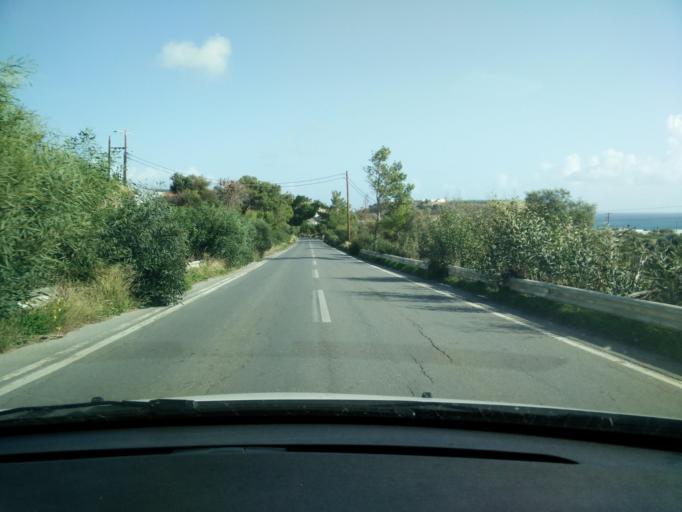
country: GR
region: Crete
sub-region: Nomos Lasithiou
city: Gra Liyia
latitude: 35.0087
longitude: 25.6278
